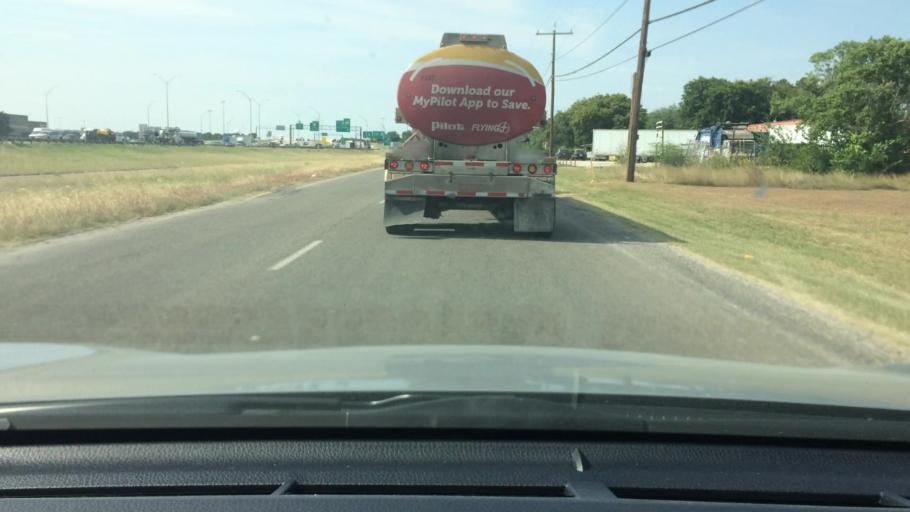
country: US
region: Texas
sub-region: Bexar County
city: Kirby
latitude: 29.4290
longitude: -98.3886
